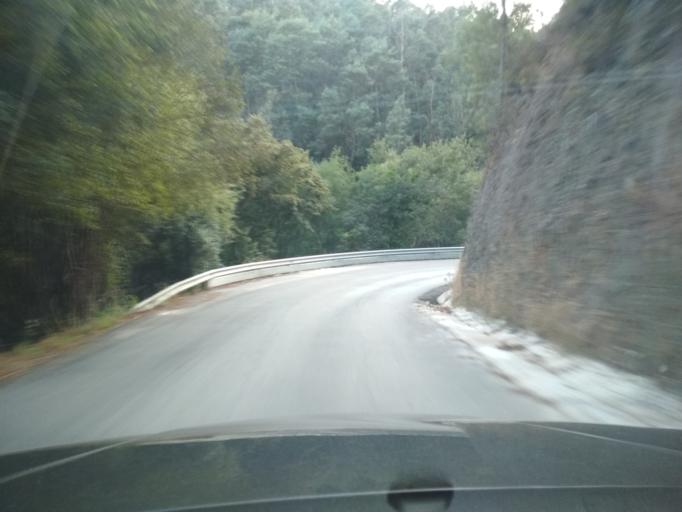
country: PT
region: Coimbra
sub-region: Coimbra
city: Coimbra
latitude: 40.2499
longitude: -8.3853
